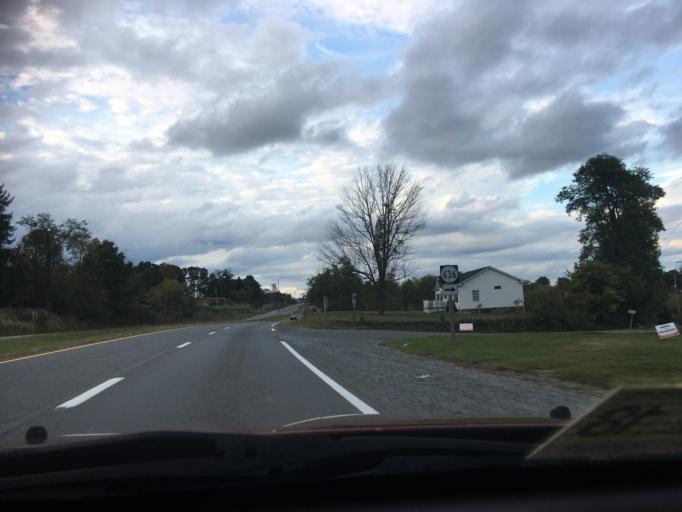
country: US
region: Virginia
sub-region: Pulaski County
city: Dublin
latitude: 37.1172
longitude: -80.6985
